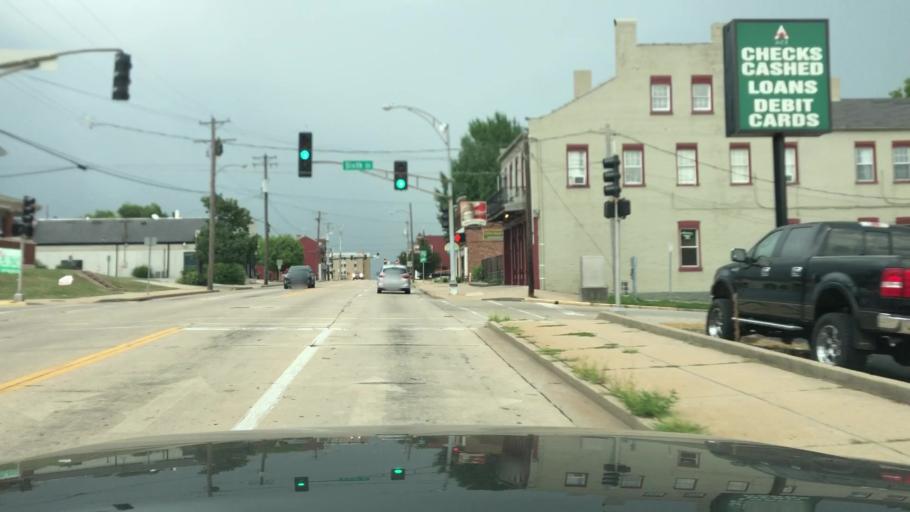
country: US
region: Missouri
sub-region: Saint Charles County
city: Saint Charles
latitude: 38.7819
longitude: -90.4896
